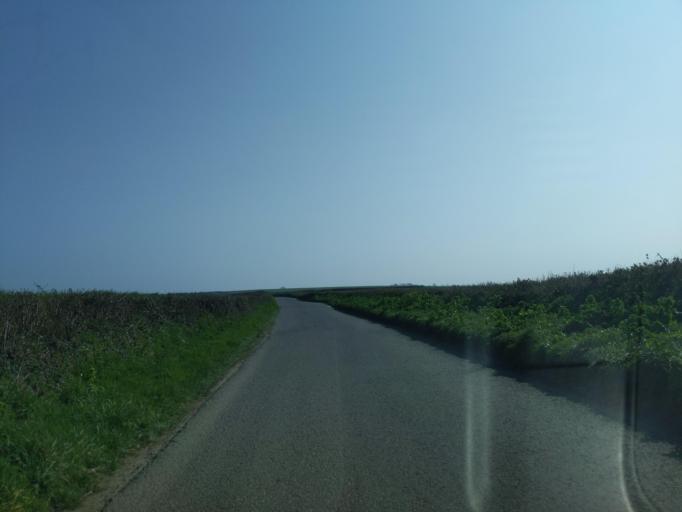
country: GB
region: England
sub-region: Devon
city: Dartmouth
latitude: 50.3399
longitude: -3.6539
